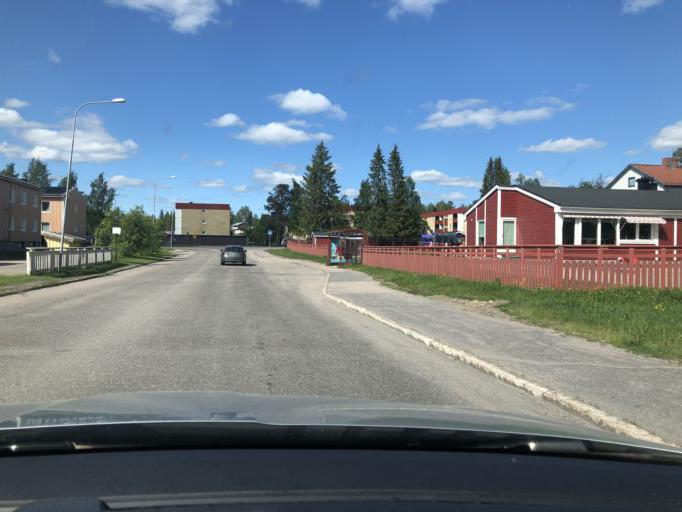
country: SE
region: Norrbotten
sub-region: Gallivare Kommun
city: Gaellivare
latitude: 67.1328
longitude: 20.6820
